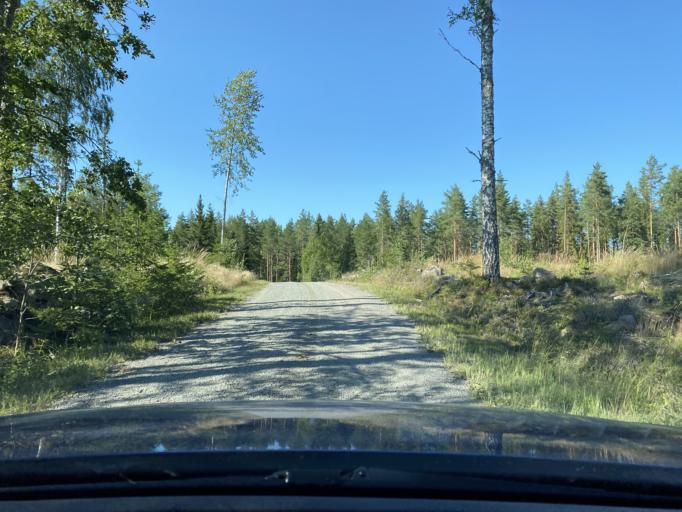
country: FI
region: Satakunta
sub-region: Rauma
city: Kiukainen
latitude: 61.1446
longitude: 22.0219
